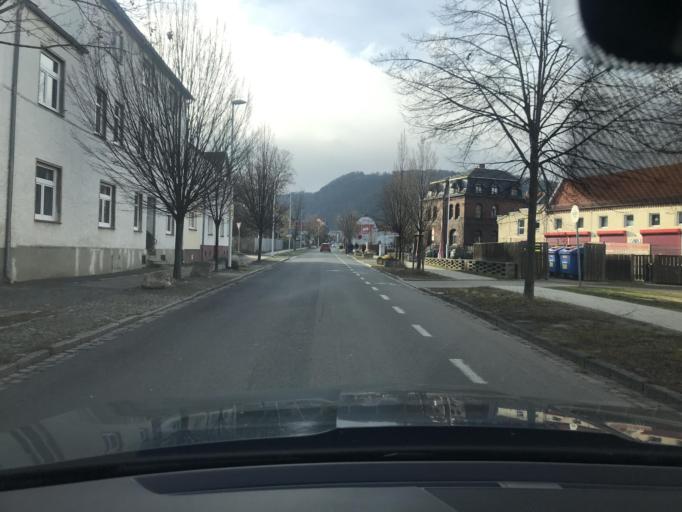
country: DE
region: Saxony-Anhalt
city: Thale
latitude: 51.7524
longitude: 11.0395
